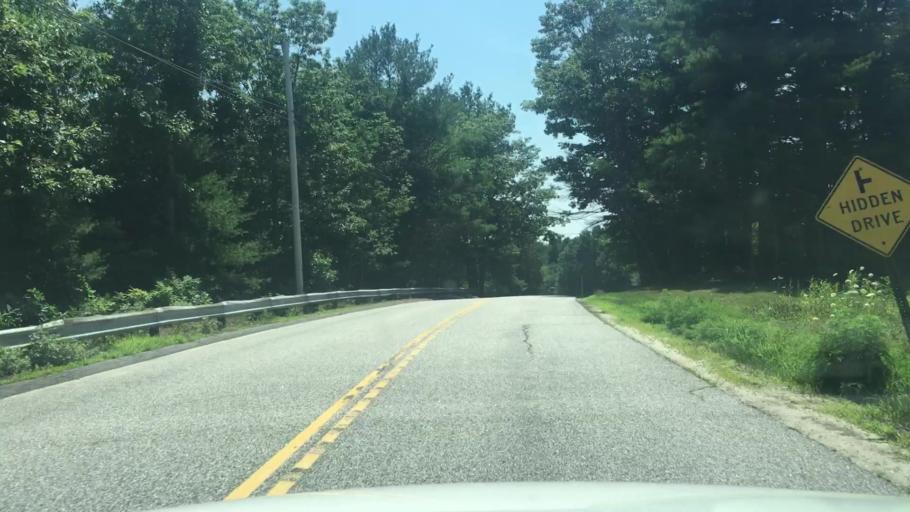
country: US
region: Maine
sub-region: Cumberland County
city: Falmouth
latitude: 43.7549
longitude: -70.2743
